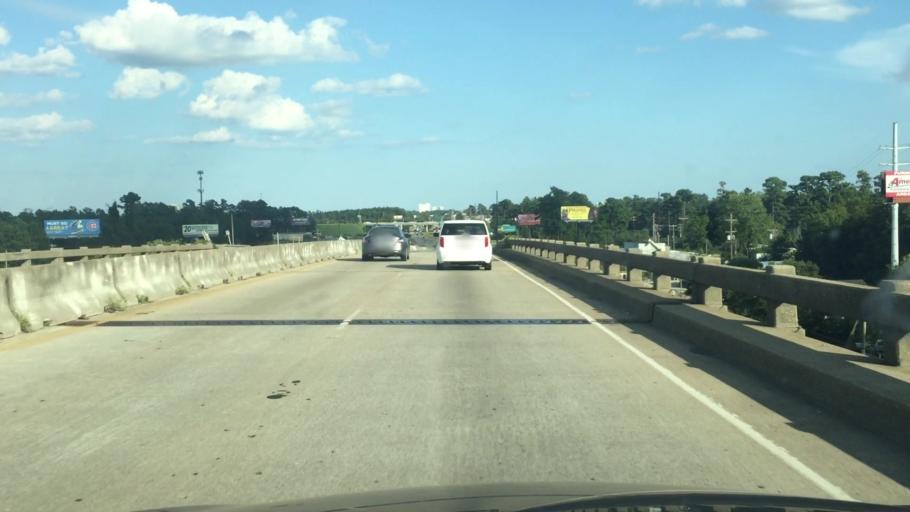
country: US
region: South Carolina
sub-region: Horry County
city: Forestbrook
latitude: 33.7140
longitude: -78.9217
